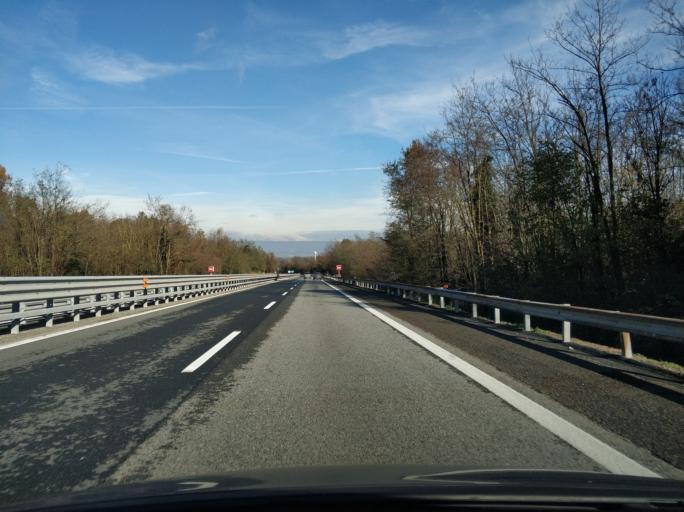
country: IT
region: Piedmont
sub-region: Provincia di Torino
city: Scarmagno
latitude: 45.3690
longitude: 7.8400
